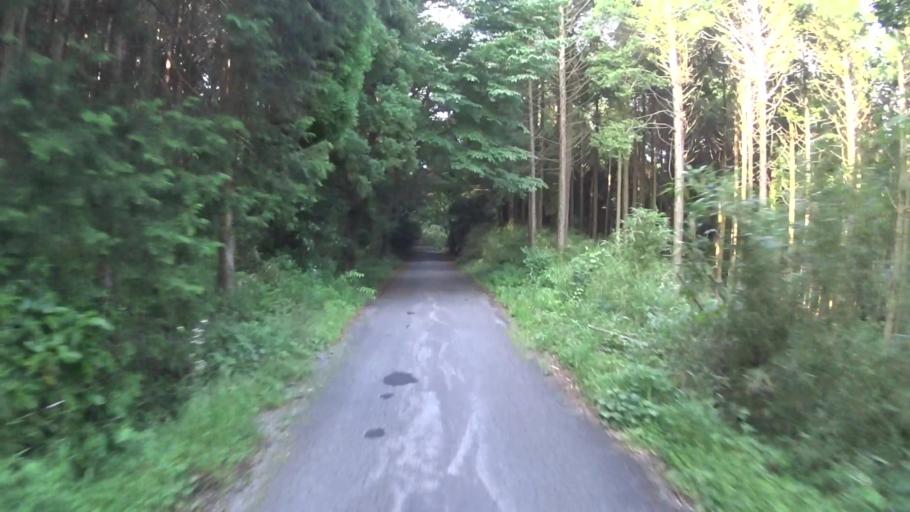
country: JP
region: Kumamoto
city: Aso
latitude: 32.9552
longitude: 131.0071
